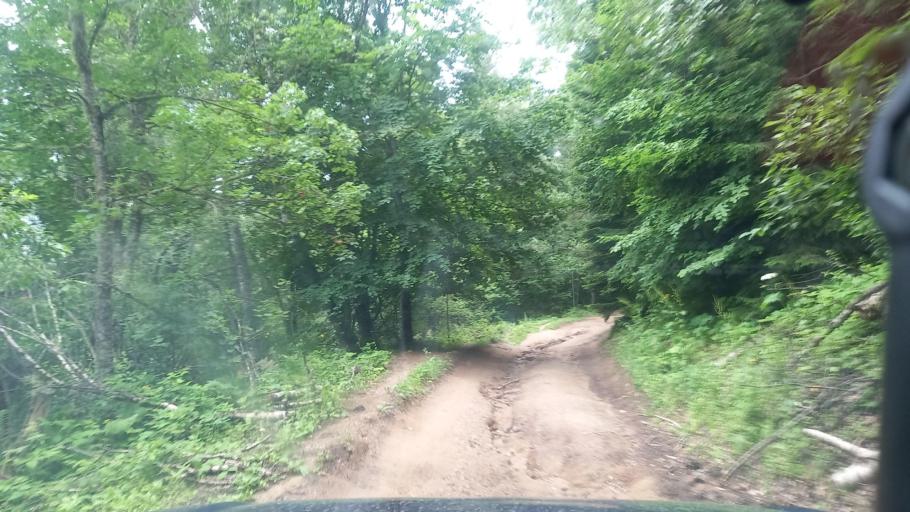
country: RU
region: Karachayevo-Cherkesiya
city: Kurdzhinovo
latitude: 43.8065
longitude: 40.8583
